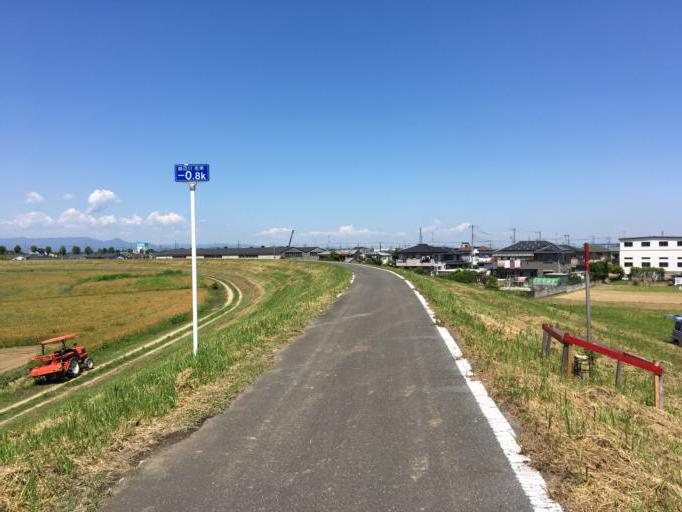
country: JP
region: Saitama
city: Kawagoe
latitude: 35.9614
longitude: 139.4774
